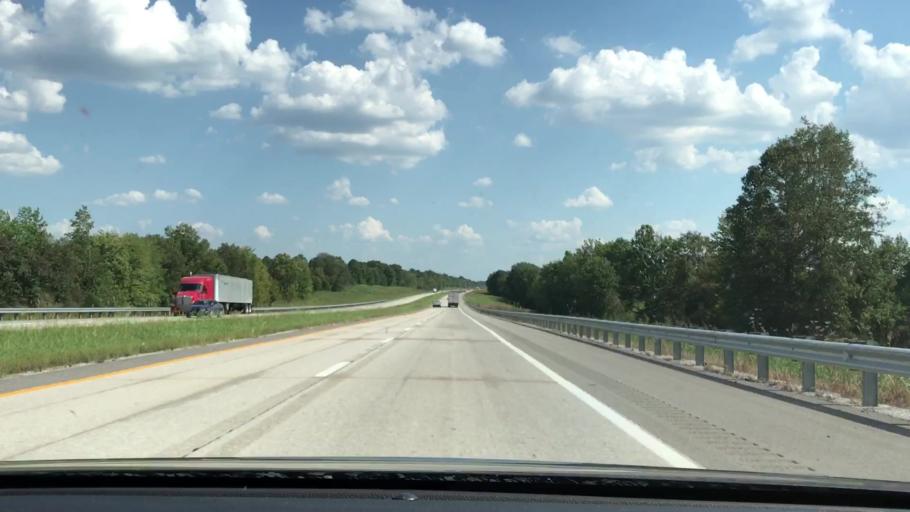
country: US
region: Kentucky
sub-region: Ohio County
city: Oak Grove
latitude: 37.3472
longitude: -86.7792
